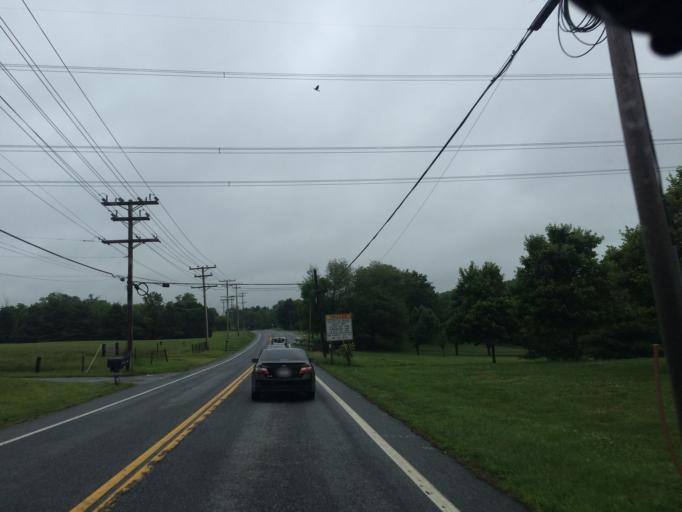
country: US
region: Maryland
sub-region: Howard County
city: Fulton
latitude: 39.1608
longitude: -76.9340
